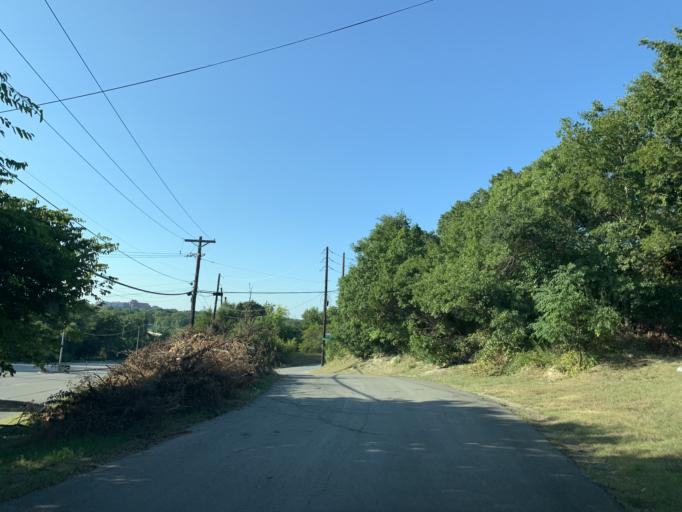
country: US
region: Texas
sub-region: Dallas County
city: Hutchins
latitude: 32.6755
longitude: -96.7847
